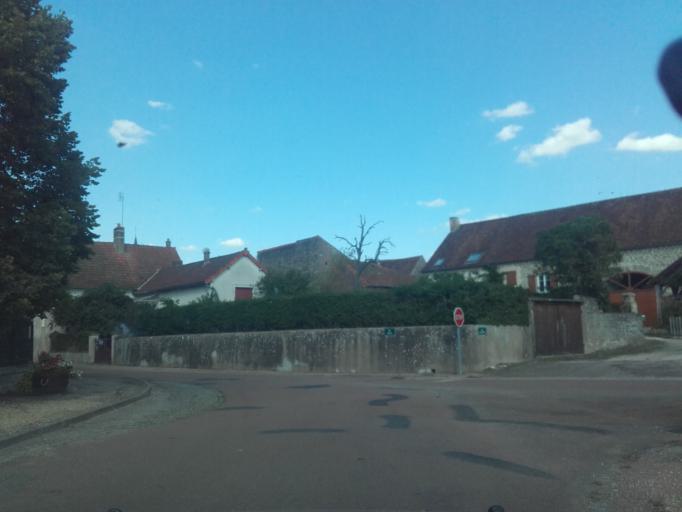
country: FR
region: Bourgogne
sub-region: Departement de Saone-et-Loire
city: Epinac
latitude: 47.0069
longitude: 4.4706
